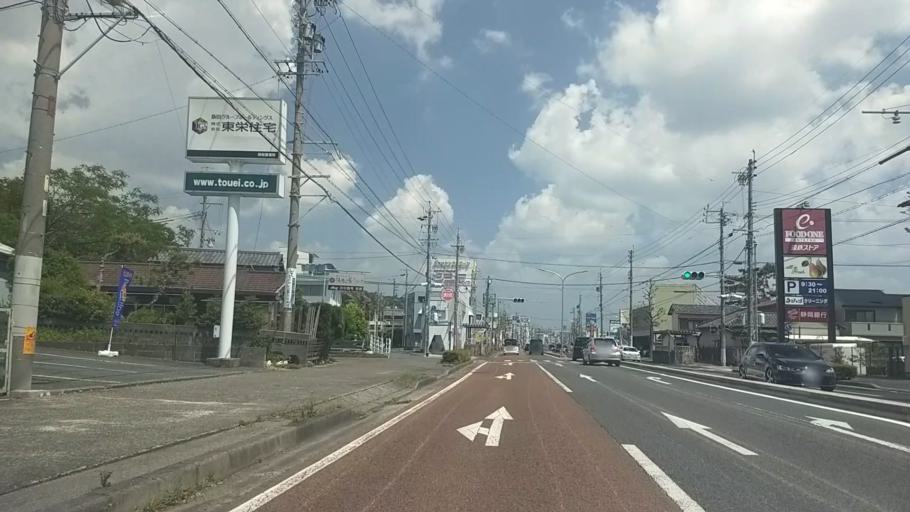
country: JP
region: Shizuoka
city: Hamamatsu
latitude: 34.7247
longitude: 137.7310
